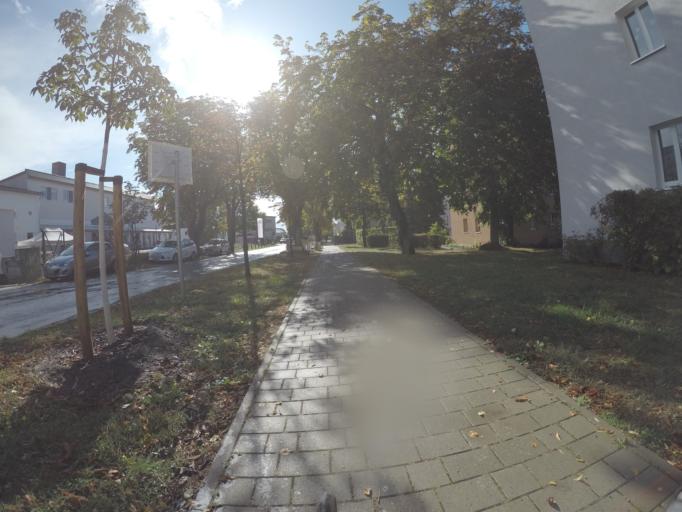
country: DE
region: Brandenburg
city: Strausberg
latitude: 52.5834
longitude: 13.8949
